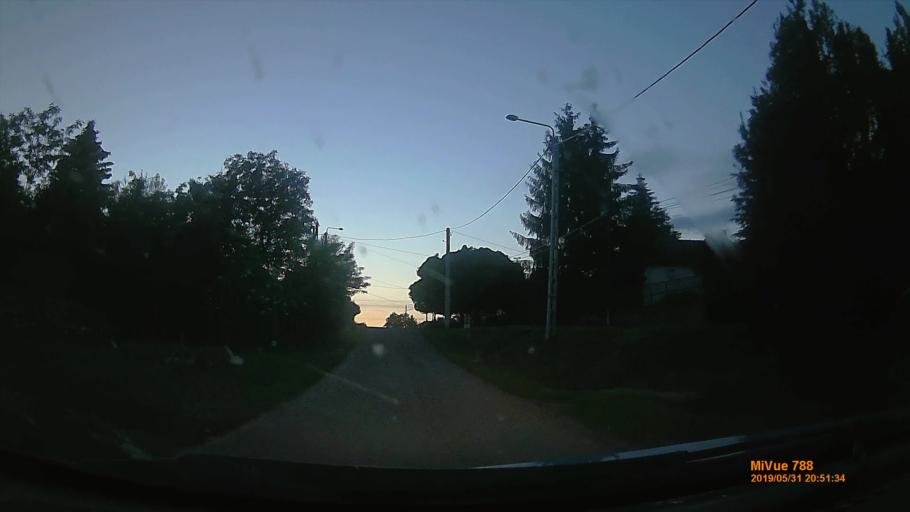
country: HU
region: Nograd
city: Nagyoroszi
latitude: 48.0430
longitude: 19.0559
